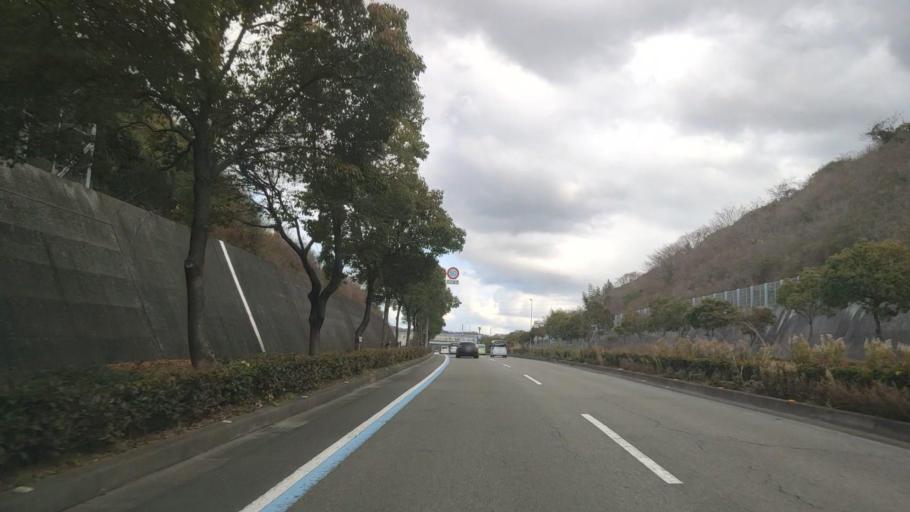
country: JP
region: Ehime
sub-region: Shikoku-chuo Shi
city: Matsuyama
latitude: 33.8892
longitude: 132.7564
